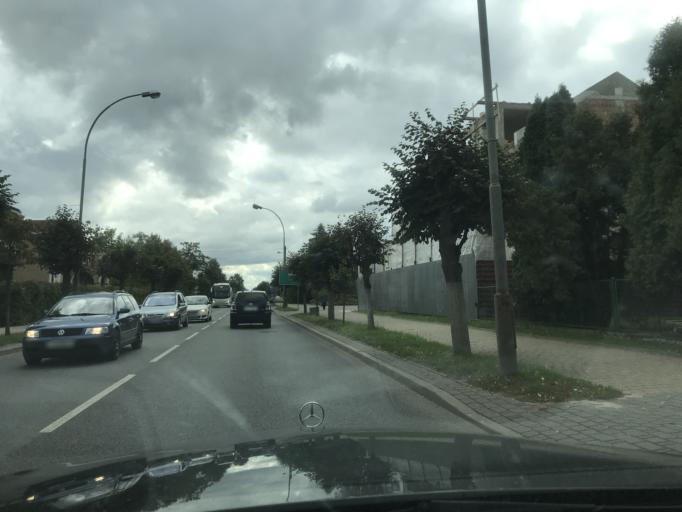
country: PL
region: Lublin Voivodeship
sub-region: Powiat janowski
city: Janow Lubelski
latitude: 50.7018
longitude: 22.4192
